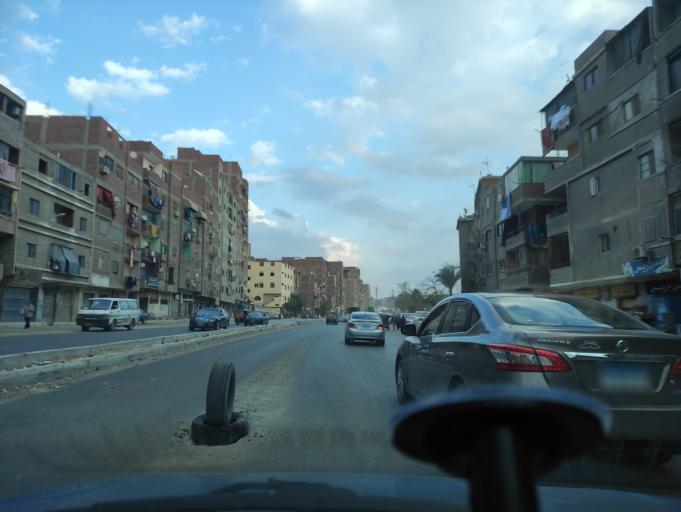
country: EG
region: Muhafazat al Qalyubiyah
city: Al Khankah
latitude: 30.1380
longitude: 31.3471
